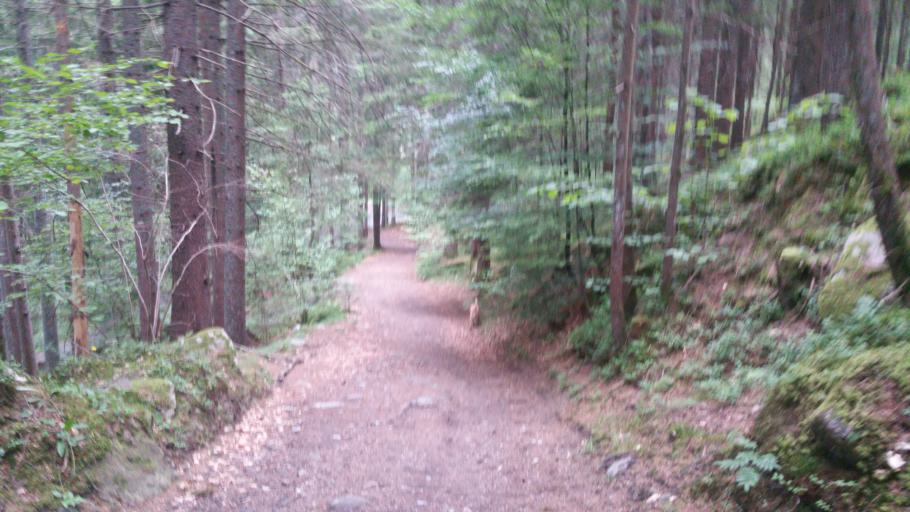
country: FR
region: Rhone-Alpes
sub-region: Departement de la Haute-Savoie
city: Les Houches
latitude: 45.9003
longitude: 6.8045
